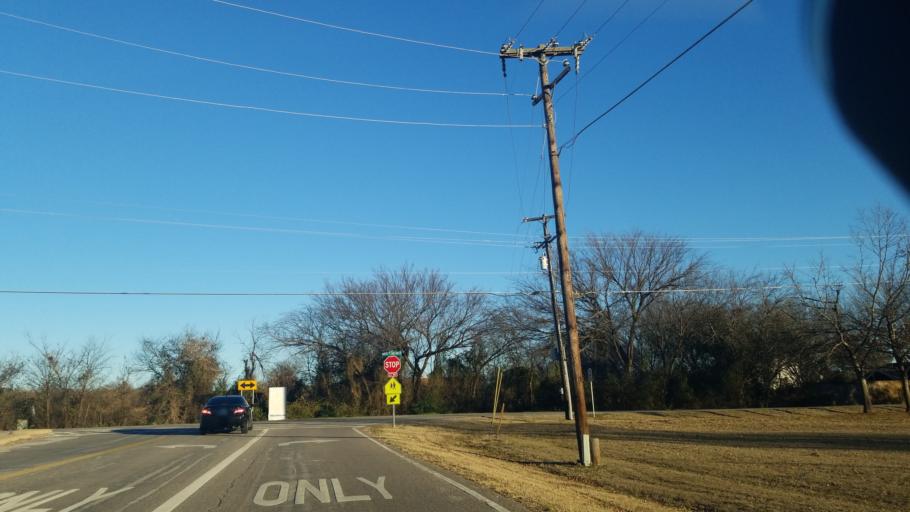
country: US
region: Texas
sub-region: Denton County
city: Shady Shores
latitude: 33.1604
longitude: -97.0408
